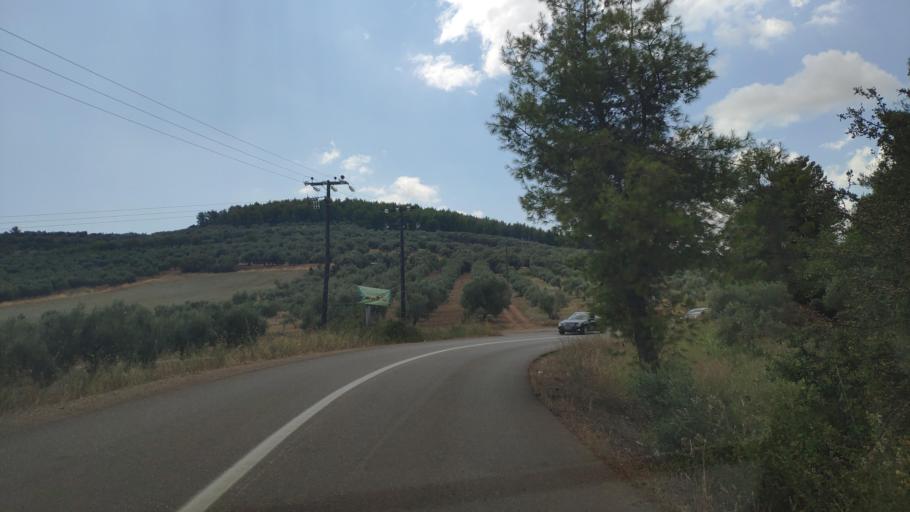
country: GR
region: Central Greece
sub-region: Nomos Fthiotidos
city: Malesina
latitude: 38.6145
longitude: 23.1844
